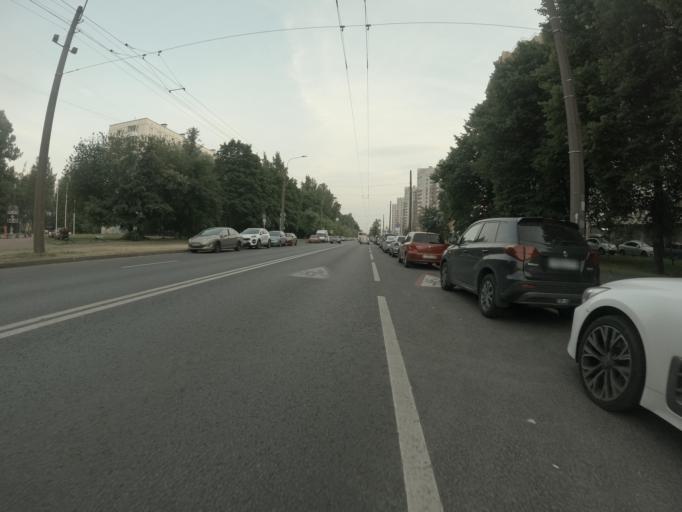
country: RU
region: Leningrad
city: Kalininskiy
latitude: 59.9837
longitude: 30.3984
